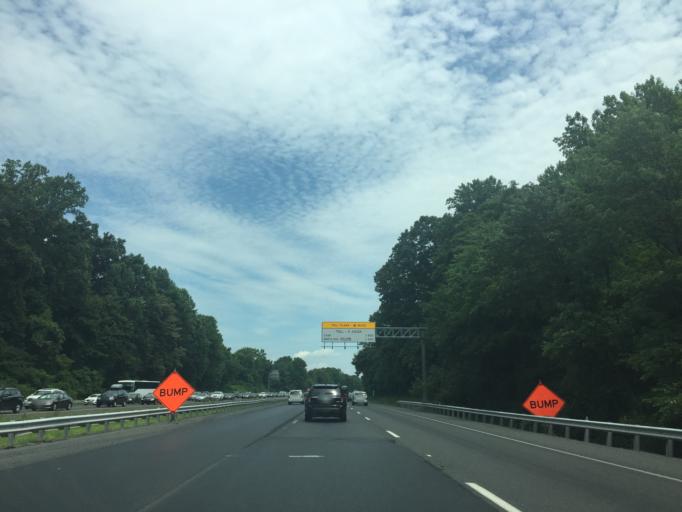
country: US
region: Maryland
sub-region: Harford County
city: Aberdeen
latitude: 39.5407
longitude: -76.1716
